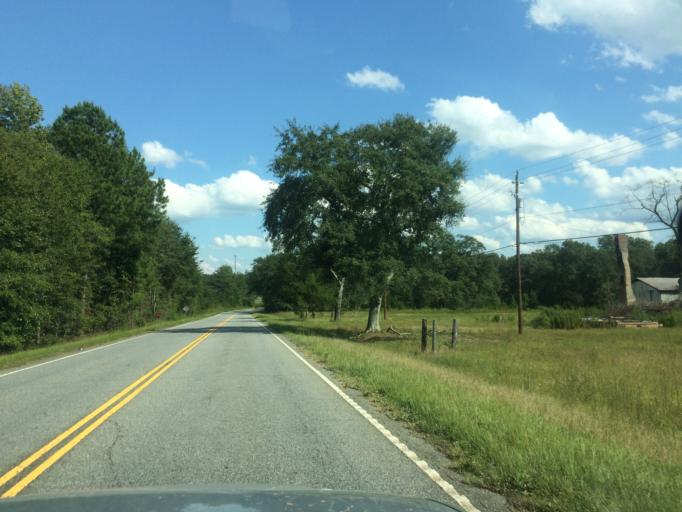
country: US
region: South Carolina
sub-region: Anderson County
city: Honea Path
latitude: 34.4734
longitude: -82.4342
